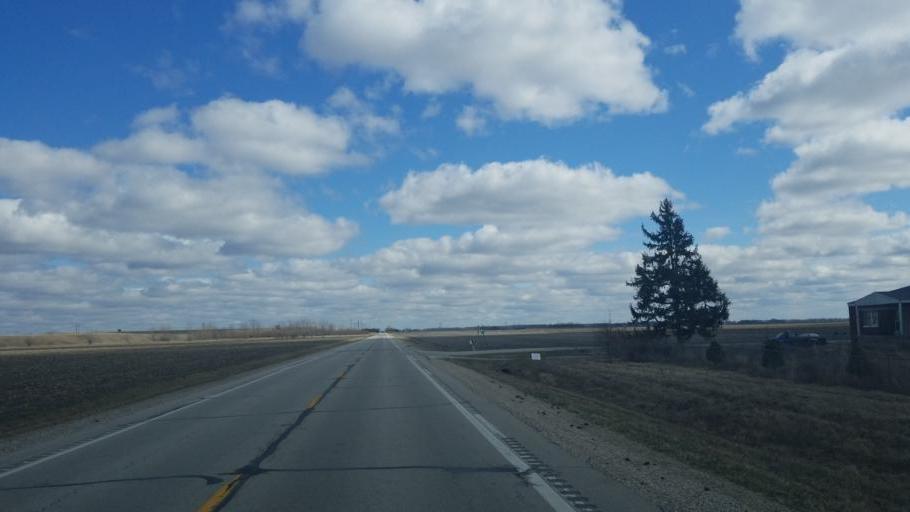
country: US
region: Illinois
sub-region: Douglas County
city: Villa Grove
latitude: 39.7922
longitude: -88.0648
